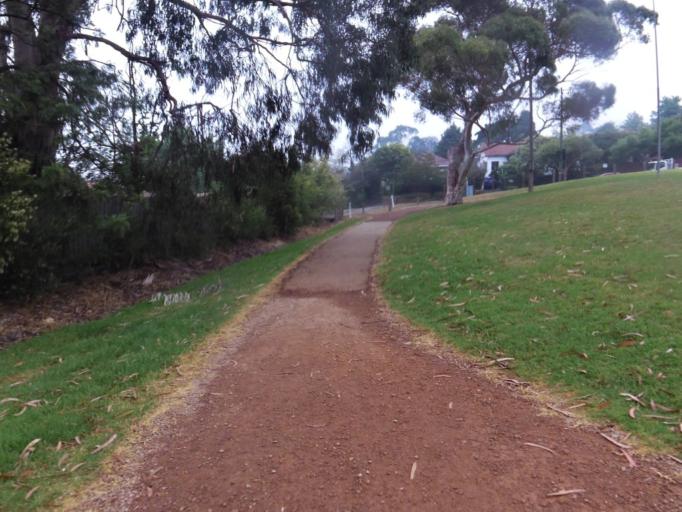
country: AU
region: Victoria
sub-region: Whitehorse
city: Box Hill South
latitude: -37.8278
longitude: 145.1181
